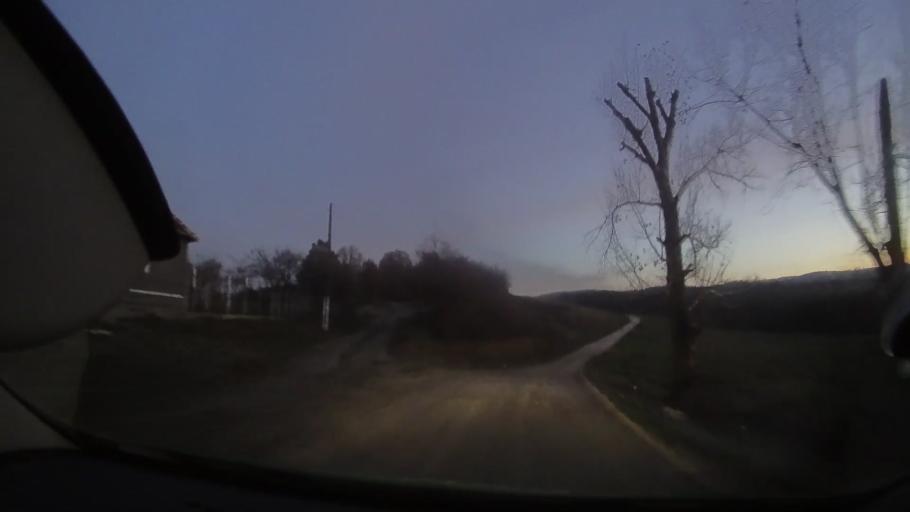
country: RO
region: Bihor
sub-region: Comuna Tetchea
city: Hotar
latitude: 47.0106
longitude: 22.3048
